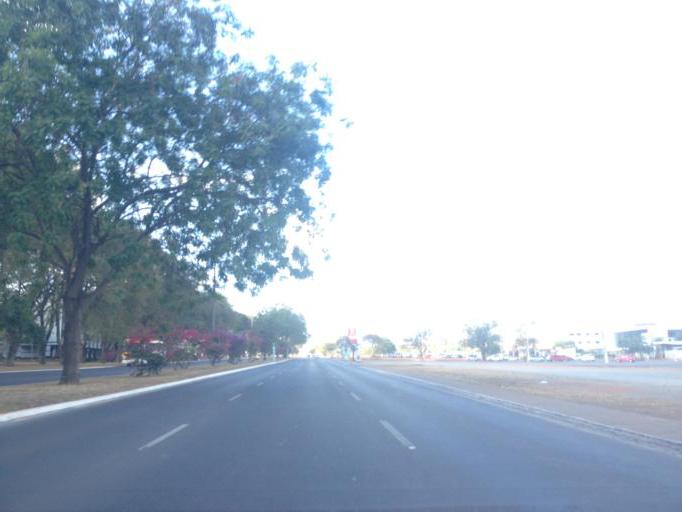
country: BR
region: Federal District
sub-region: Brasilia
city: Brasilia
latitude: -15.8346
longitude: -47.9139
